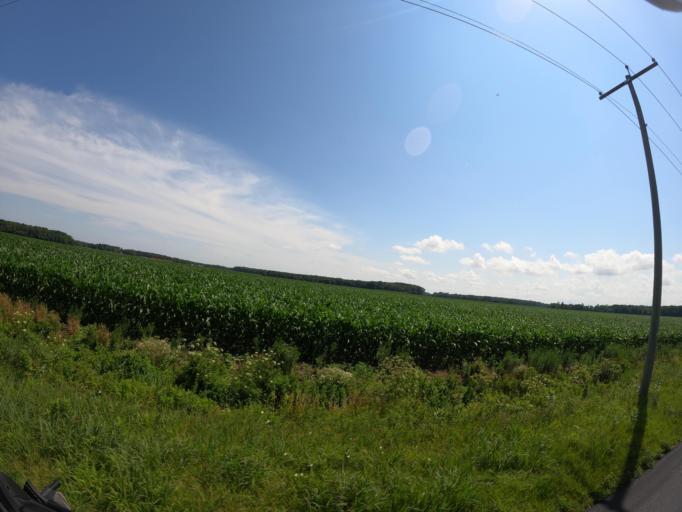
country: US
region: Maryland
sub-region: Worcester County
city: Ocean Pines
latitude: 38.4514
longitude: -75.1625
